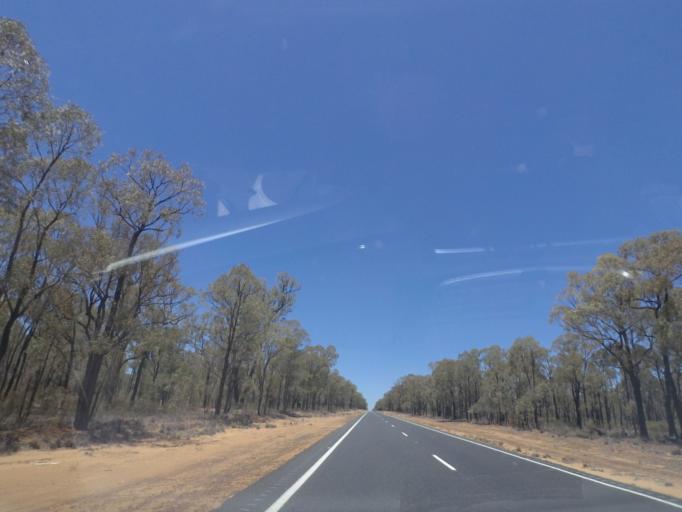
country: AU
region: New South Wales
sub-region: Narrabri
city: Narrabri
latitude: -30.7285
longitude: 149.5217
